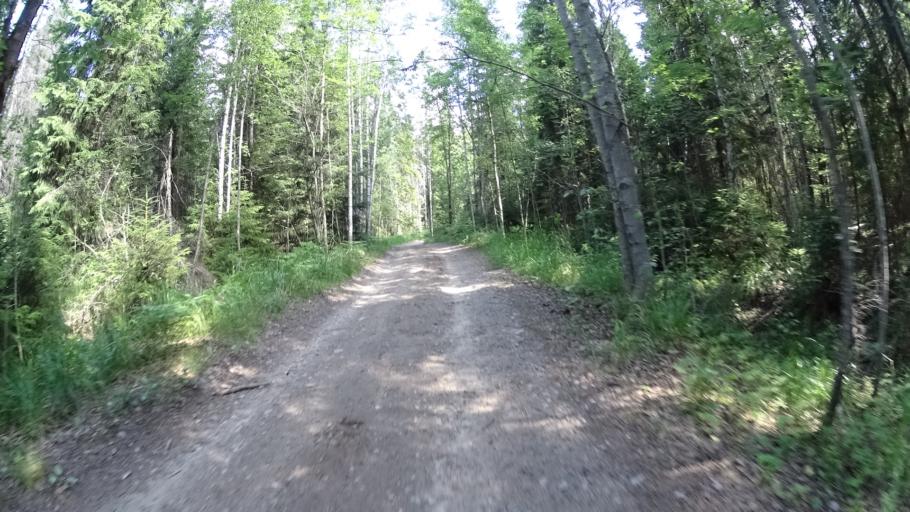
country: FI
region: Uusimaa
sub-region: Helsinki
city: Vihti
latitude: 60.3291
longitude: 24.4662
